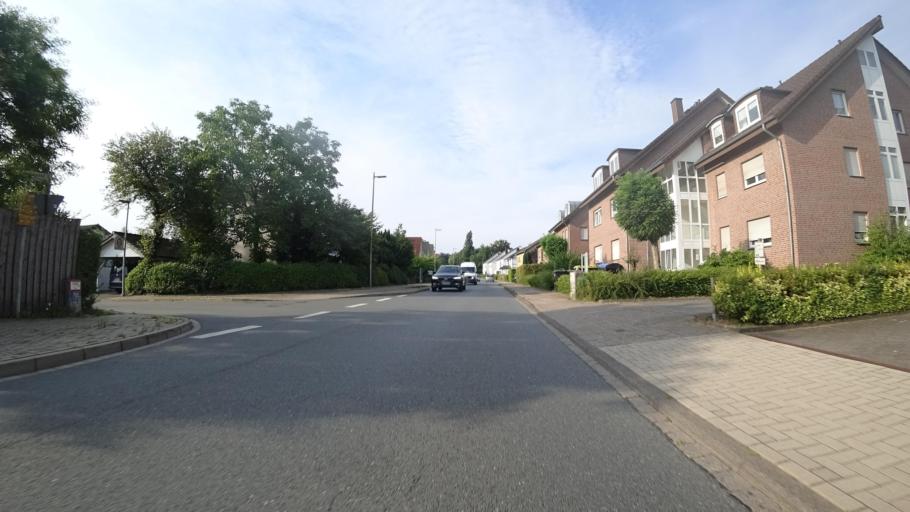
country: DE
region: North Rhine-Westphalia
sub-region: Regierungsbezirk Detmold
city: Werther
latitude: 52.0362
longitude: 8.4630
